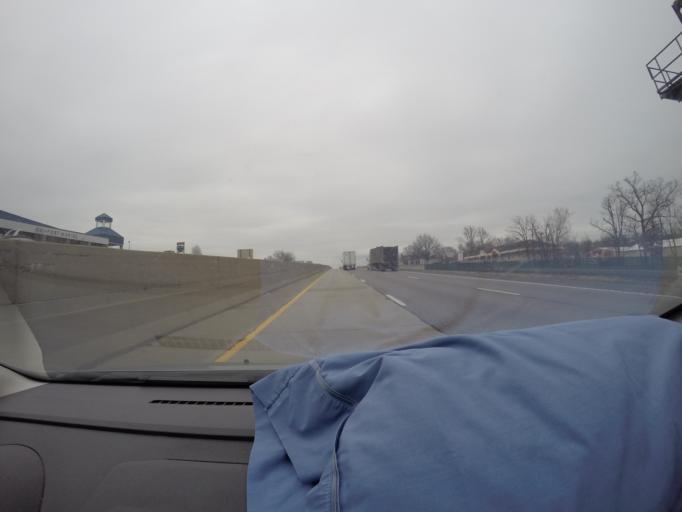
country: US
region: Missouri
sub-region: Saint Charles County
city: Lake Saint Louis
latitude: 38.8037
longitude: -90.7580
